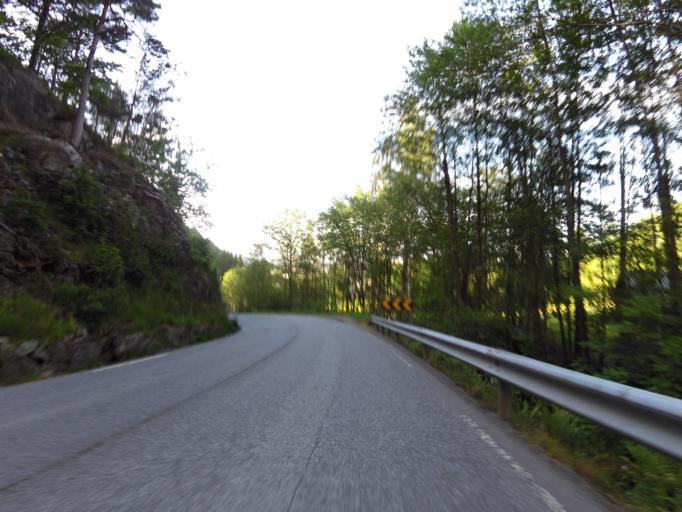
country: NO
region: Vest-Agder
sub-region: Flekkefjord
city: Flekkefjord
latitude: 58.2841
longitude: 6.6445
